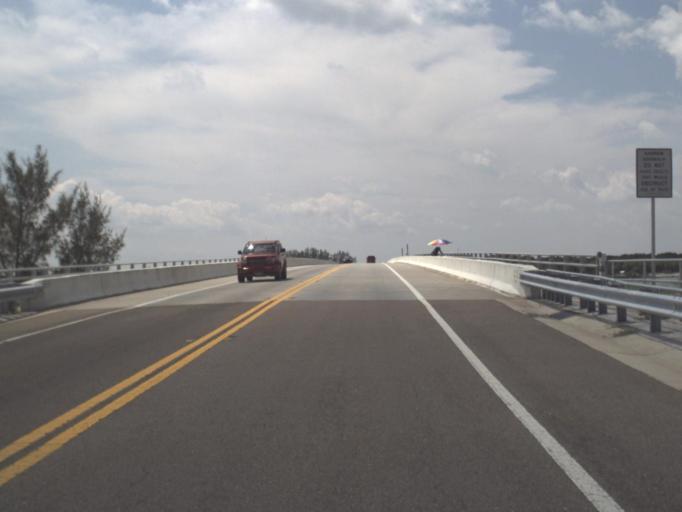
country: US
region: Florida
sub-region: Pinellas County
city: Tierra Verde
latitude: 27.6517
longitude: -82.7164
